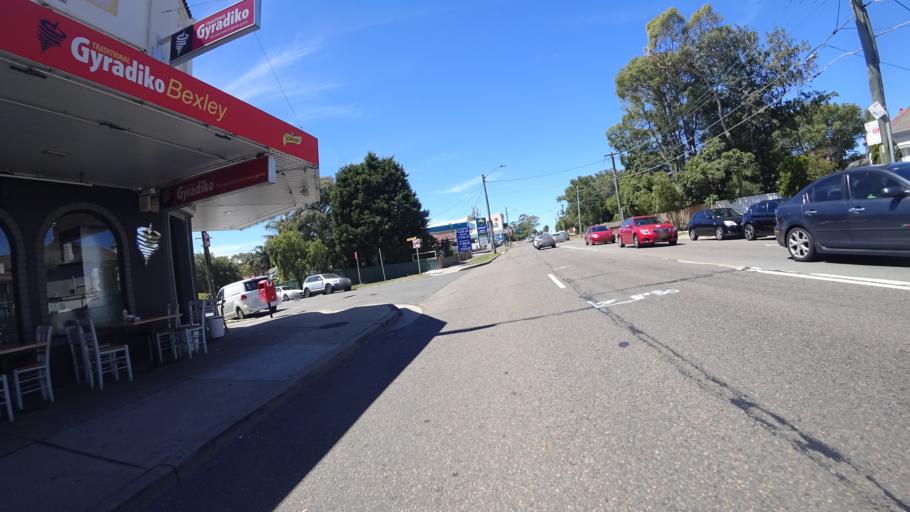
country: AU
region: New South Wales
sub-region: Rockdale
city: Bexley
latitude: -33.9452
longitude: 151.1282
